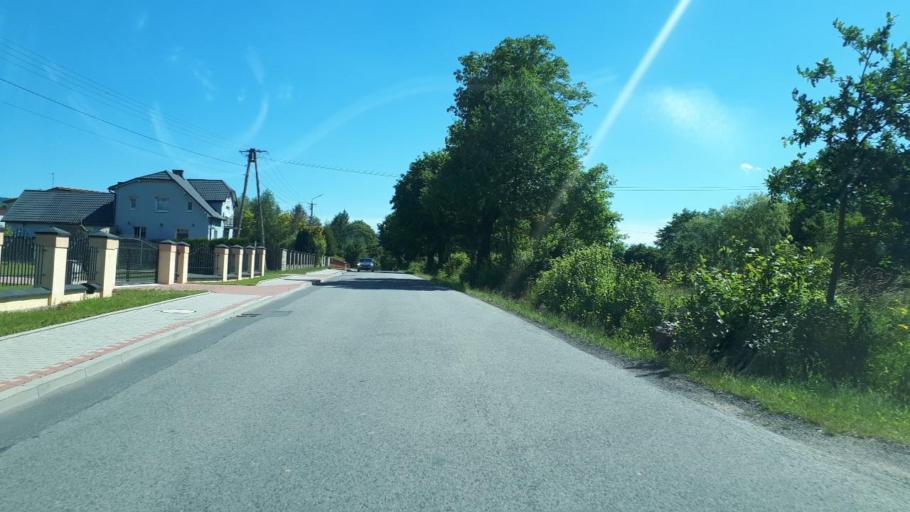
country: PL
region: Silesian Voivodeship
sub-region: Powiat zywiecki
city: Lodygowice
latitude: 49.7147
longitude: 19.1362
